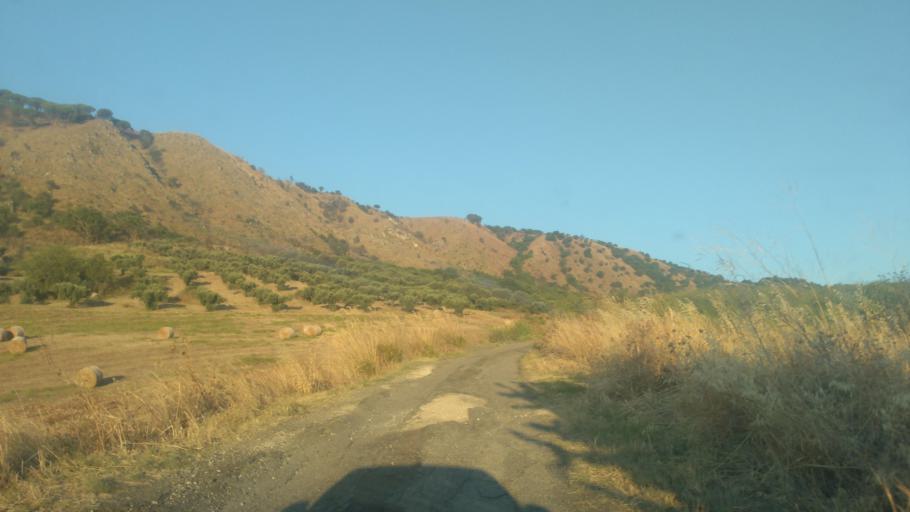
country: IT
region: Calabria
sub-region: Provincia di Catanzaro
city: Squillace Lido
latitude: 38.7725
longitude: 16.5546
